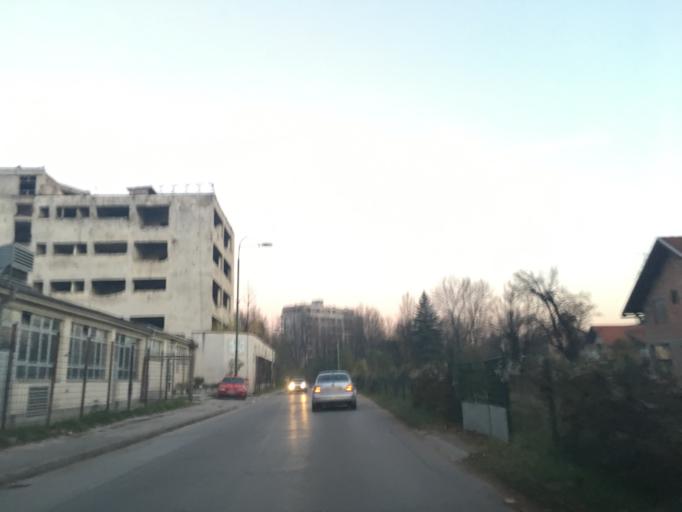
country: BA
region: Federation of Bosnia and Herzegovina
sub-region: Kanton Sarajevo
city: Sarajevo
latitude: 43.8233
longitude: 18.3044
